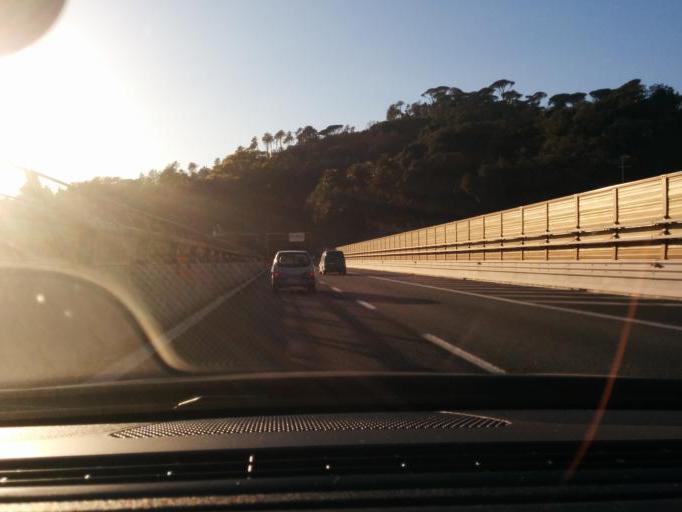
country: IT
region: Liguria
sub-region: Provincia di Genova
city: Mele
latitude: 44.4303
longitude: 8.8198
